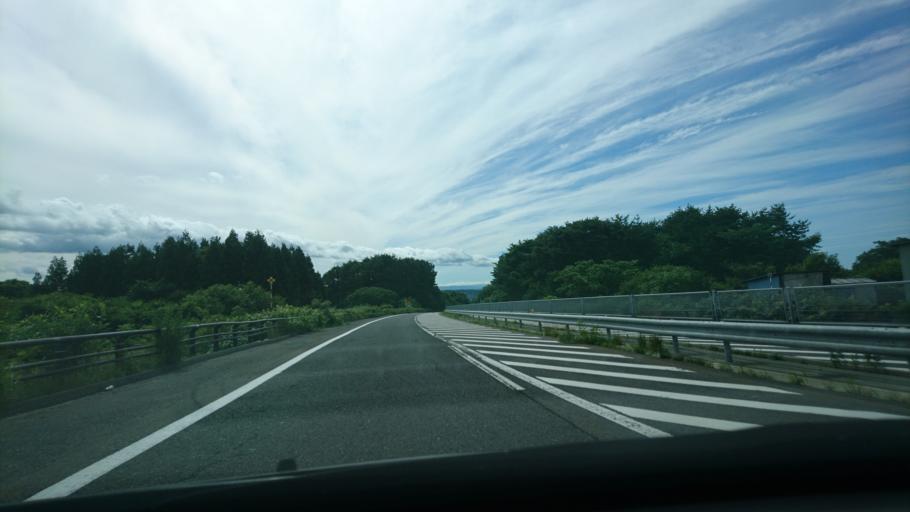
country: JP
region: Aomori
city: Hachinohe
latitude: 40.4793
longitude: 141.5484
